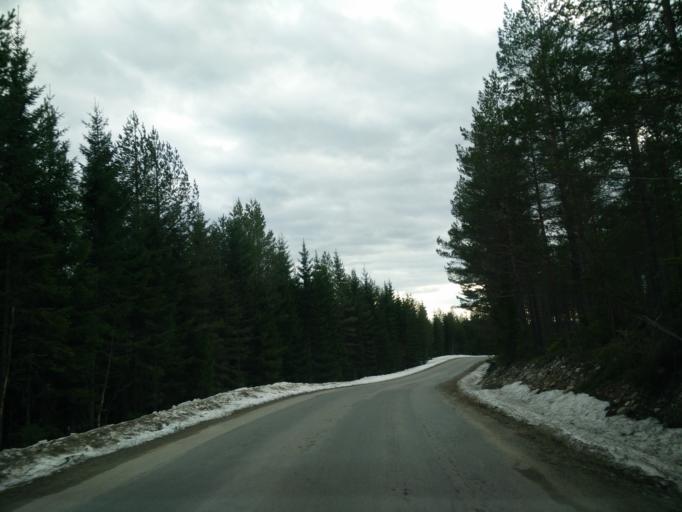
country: SE
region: Vaesternorrland
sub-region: Haernoesands Kommun
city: Haernoesand
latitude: 62.7122
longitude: 18.0455
